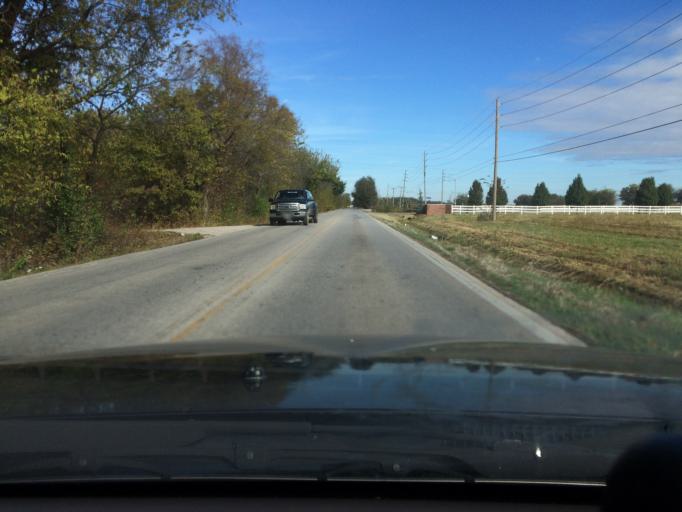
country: US
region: Oklahoma
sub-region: Tulsa County
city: Broken Arrow
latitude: 36.1096
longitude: -95.7617
